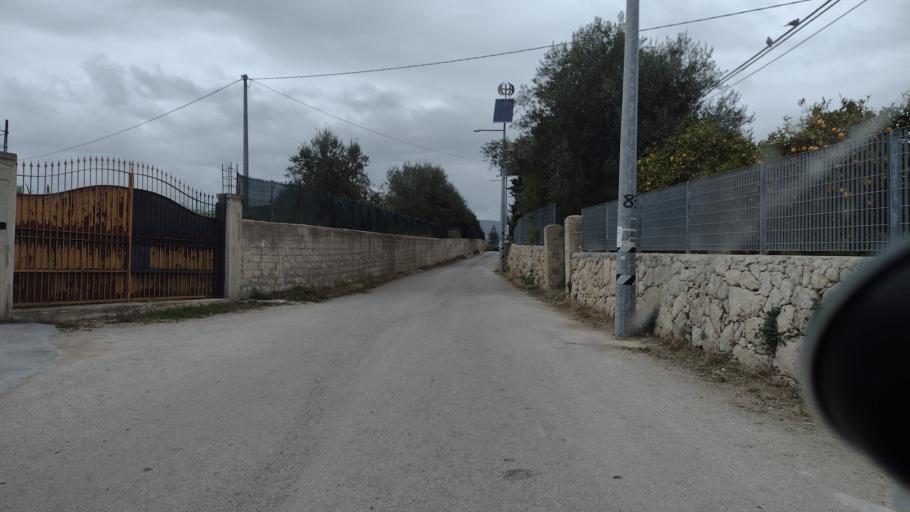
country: IT
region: Sicily
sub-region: Provincia di Siracusa
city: Avola
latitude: 36.8949
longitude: 15.1153
